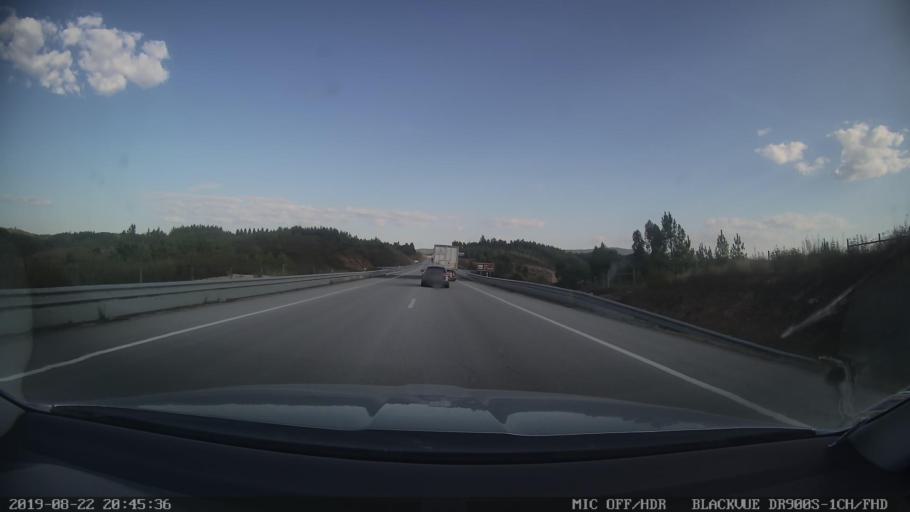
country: PT
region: Castelo Branco
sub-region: Proenca-A-Nova
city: Proenca-a-Nova
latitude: 39.7183
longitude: -7.8679
